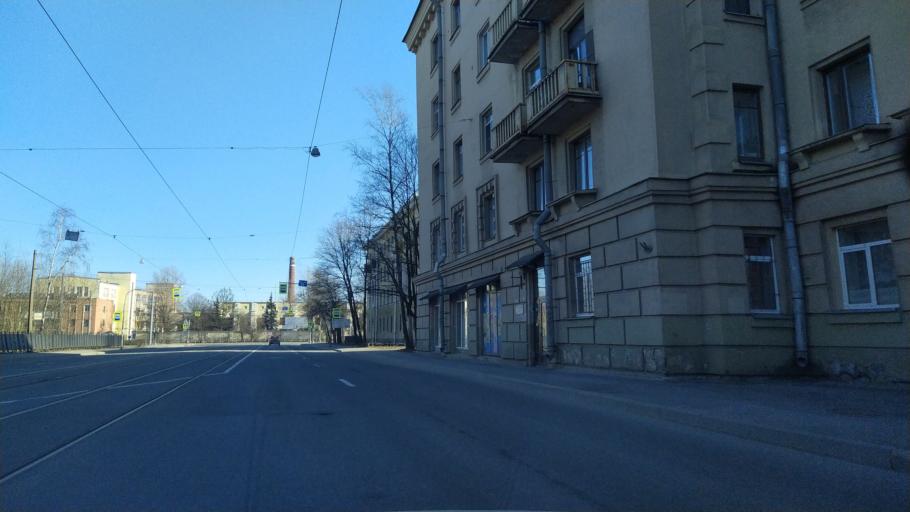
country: RU
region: St.-Petersburg
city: Centralniy
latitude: 59.9008
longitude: 30.3695
